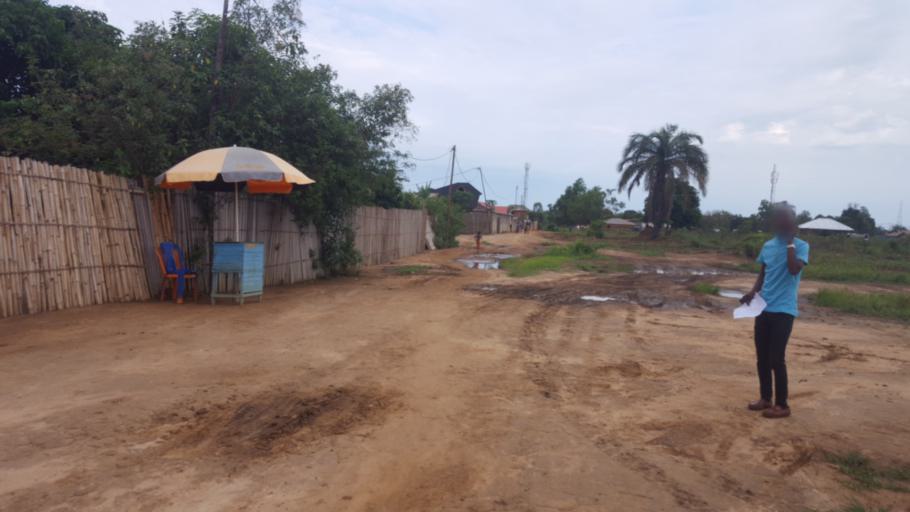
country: CD
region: Bandundu
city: Bandundu
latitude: -3.3021
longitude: 17.3786
